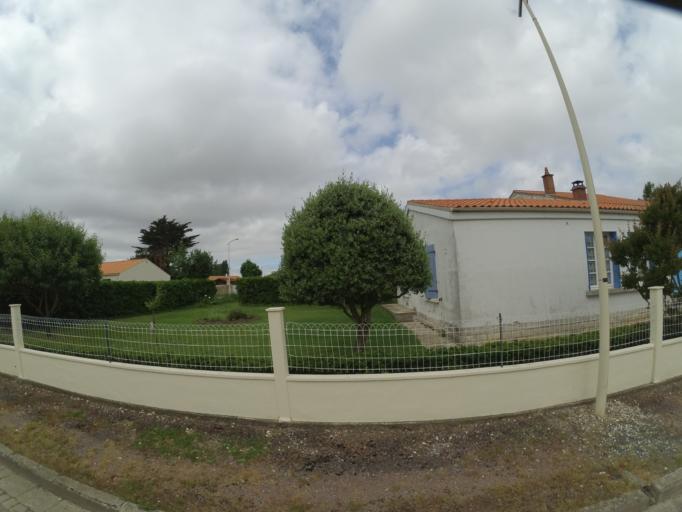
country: FR
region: Poitou-Charentes
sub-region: Departement de la Charente-Maritime
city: Yves
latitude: 46.0197
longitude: -1.0478
